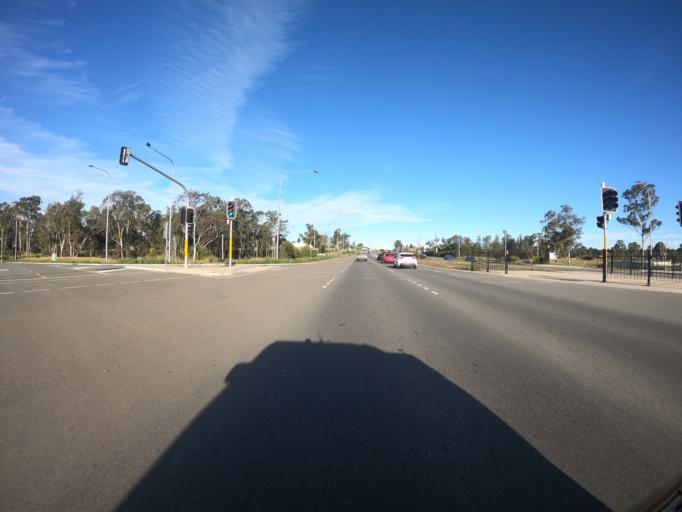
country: AU
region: New South Wales
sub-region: Blacktown
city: Hassall Grove
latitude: -33.7007
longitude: 150.8346
